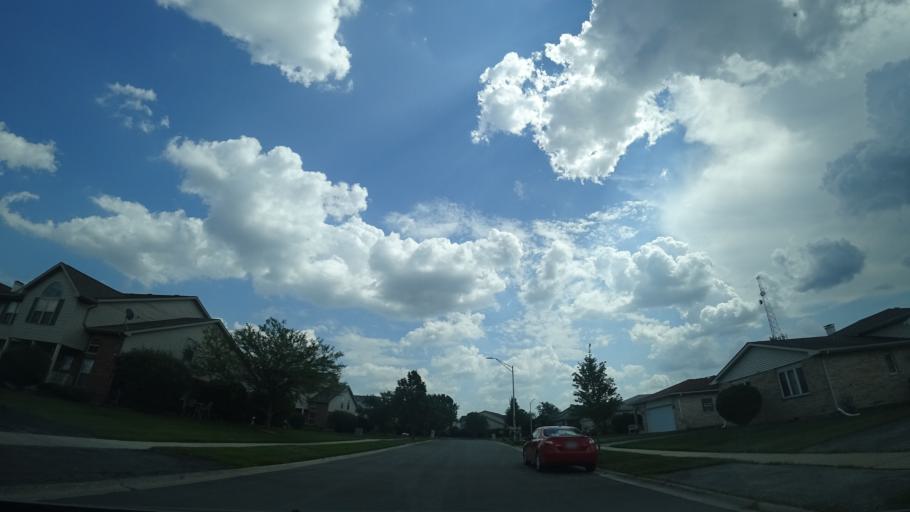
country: US
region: Illinois
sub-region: Cook County
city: Merrionette Park
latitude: 41.6663
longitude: -87.7134
